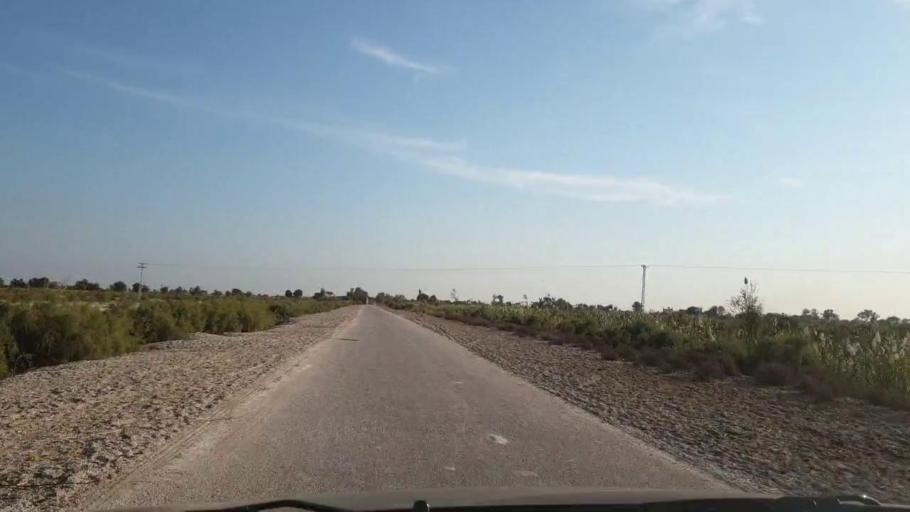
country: PK
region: Sindh
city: Khadro
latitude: 26.2059
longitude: 68.7467
